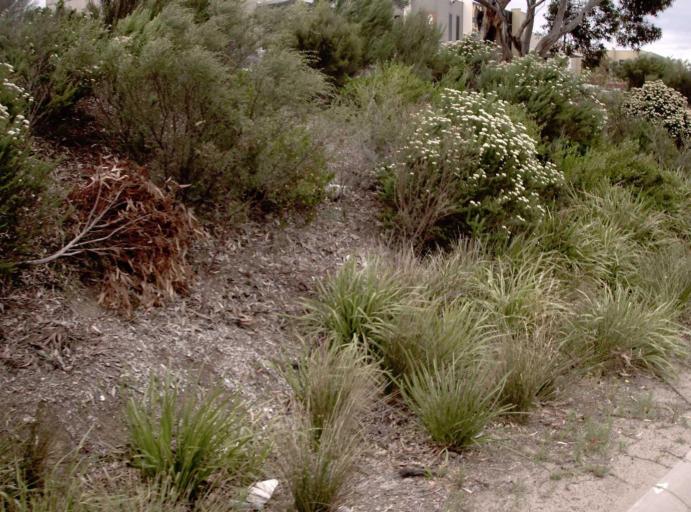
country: AU
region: Victoria
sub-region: Casey
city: Hampton Park
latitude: -38.0315
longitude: 145.2444
